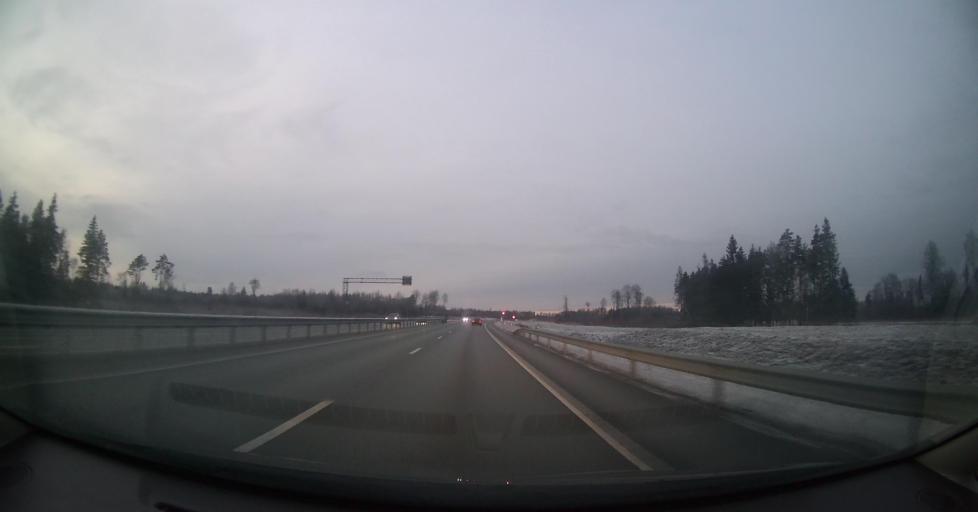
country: EE
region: Jaervamaa
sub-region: Paide linn
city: Paide
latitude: 59.0347
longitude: 25.4577
